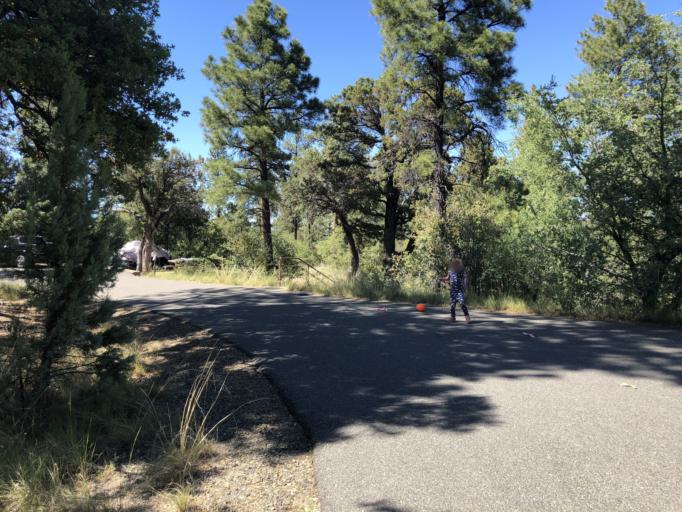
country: US
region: Arizona
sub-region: Yavapai County
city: Prescott
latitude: 34.5169
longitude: -112.3884
